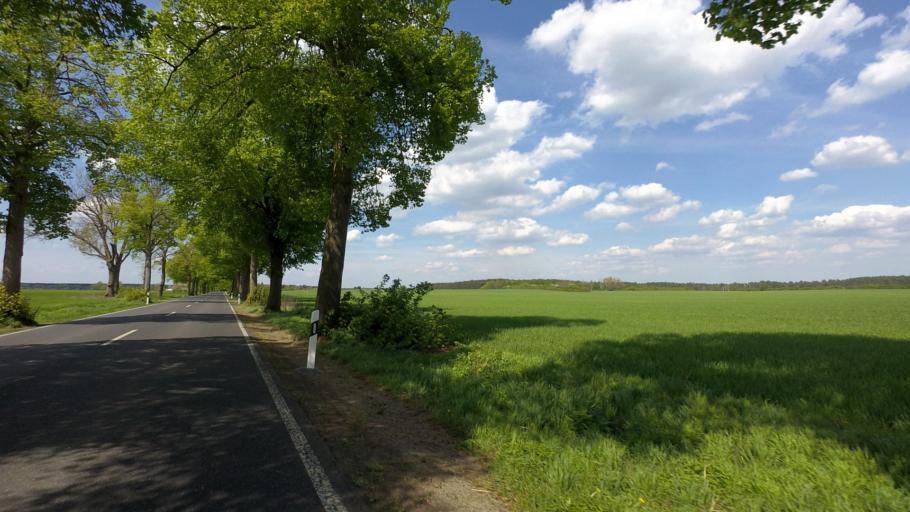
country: DE
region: Brandenburg
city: Marienwerder
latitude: 52.8914
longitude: 13.5421
